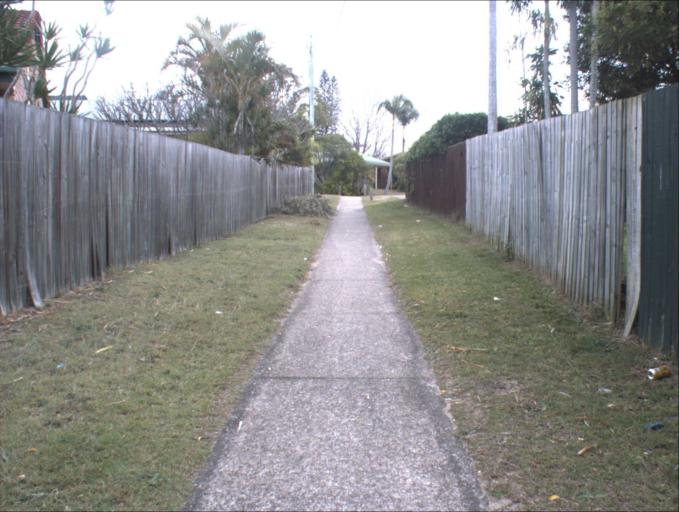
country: AU
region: Queensland
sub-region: Logan
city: Park Ridge South
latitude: -27.6806
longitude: 153.0484
